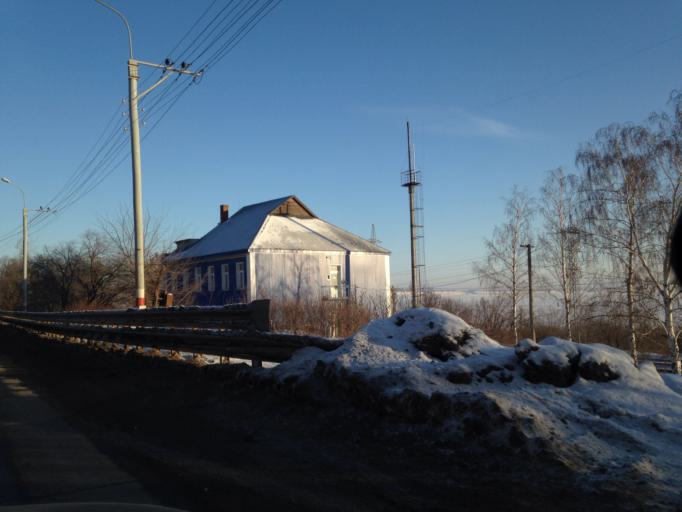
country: RU
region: Ulyanovsk
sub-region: Ulyanovskiy Rayon
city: Ulyanovsk
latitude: 54.3058
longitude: 48.4018
